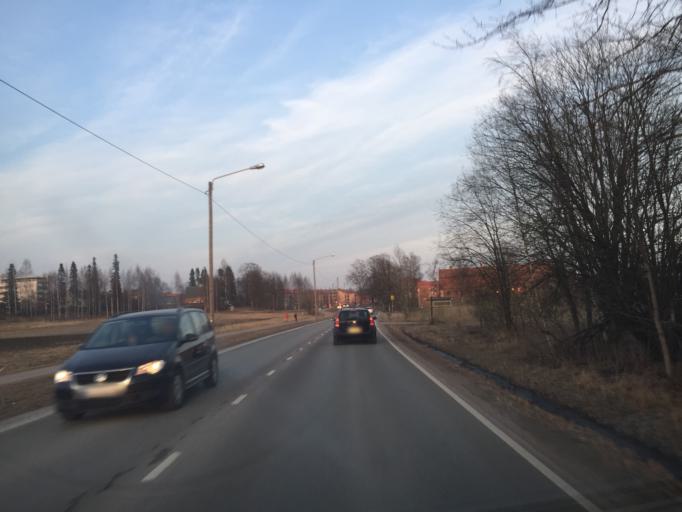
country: FI
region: Uusimaa
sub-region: Helsinki
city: Vantaa
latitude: 60.2861
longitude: 24.9508
